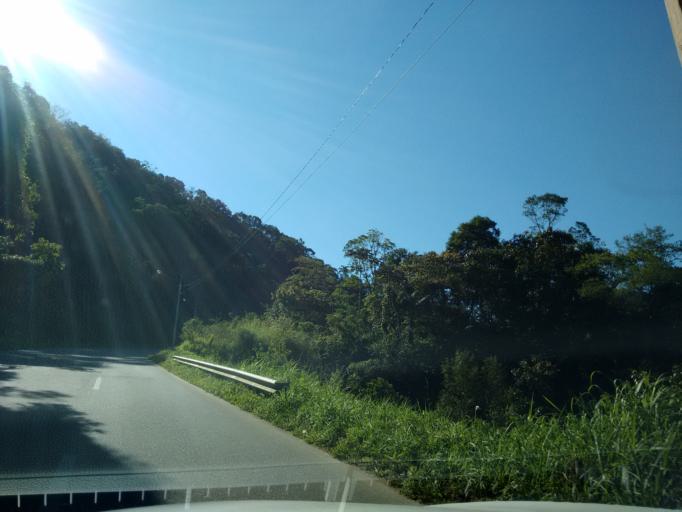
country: BR
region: Santa Catarina
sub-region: Pomerode
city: Pomerode
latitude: -26.6618
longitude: -49.1432
